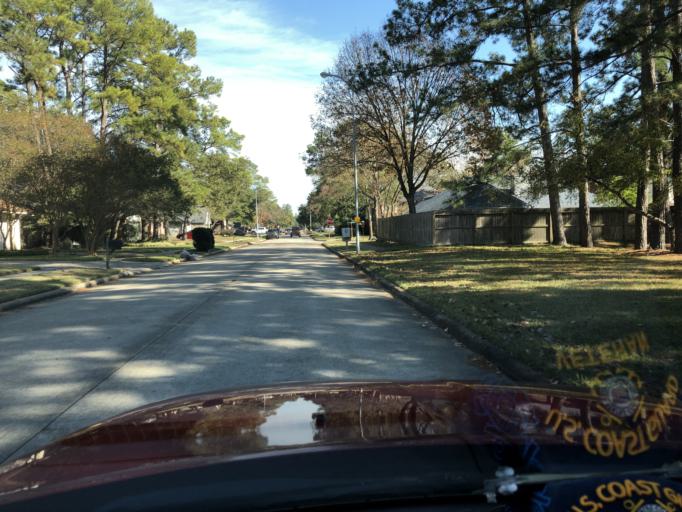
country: US
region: Texas
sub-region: Harris County
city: Tomball
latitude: 30.0195
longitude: -95.5604
